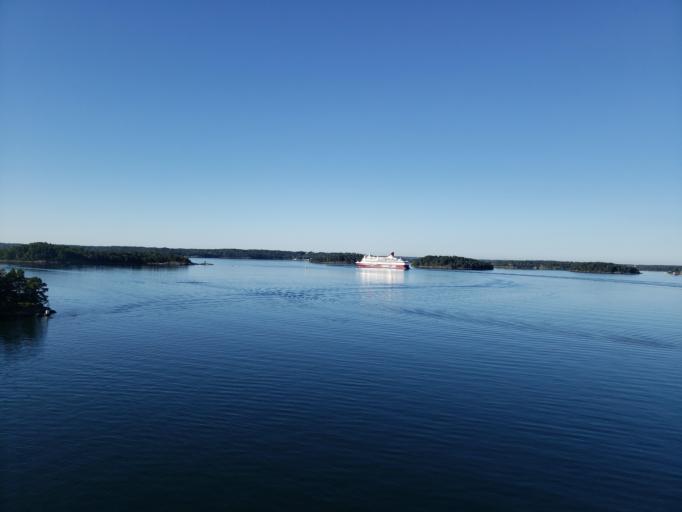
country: SE
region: Stockholm
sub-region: Vaxholms Kommun
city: Vaxholm
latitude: 59.4411
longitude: 18.3976
